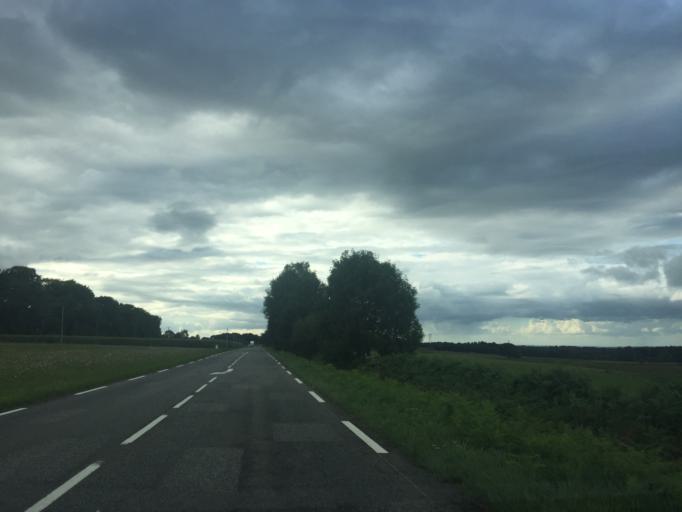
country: FR
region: Midi-Pyrenees
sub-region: Departement des Hautes-Pyrenees
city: Capvern
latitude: 43.0842
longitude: 0.3456
